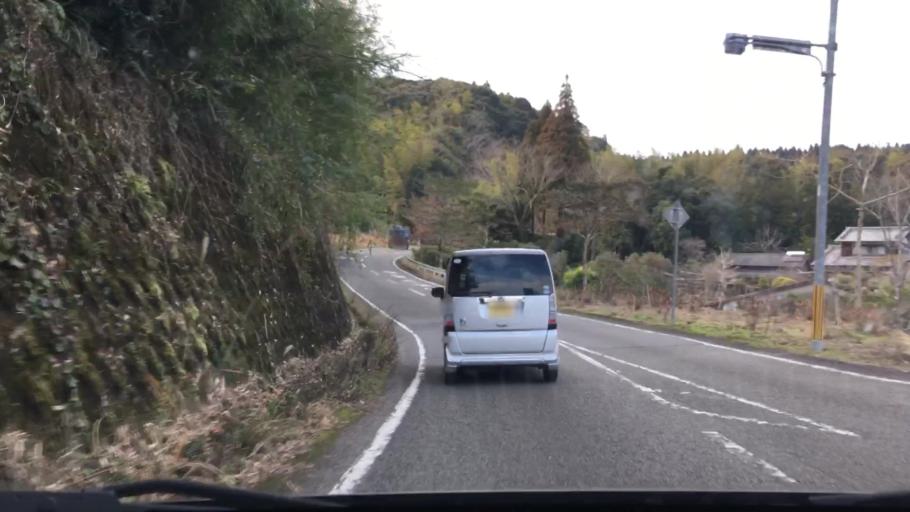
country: JP
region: Miyazaki
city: Nichinan
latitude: 31.6298
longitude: 131.3409
